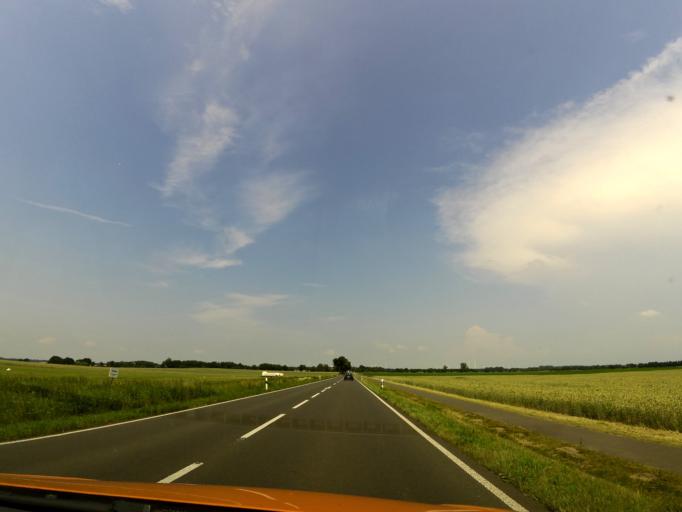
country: DE
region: Brandenburg
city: Pritzwalk
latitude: 53.1799
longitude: 12.1912
